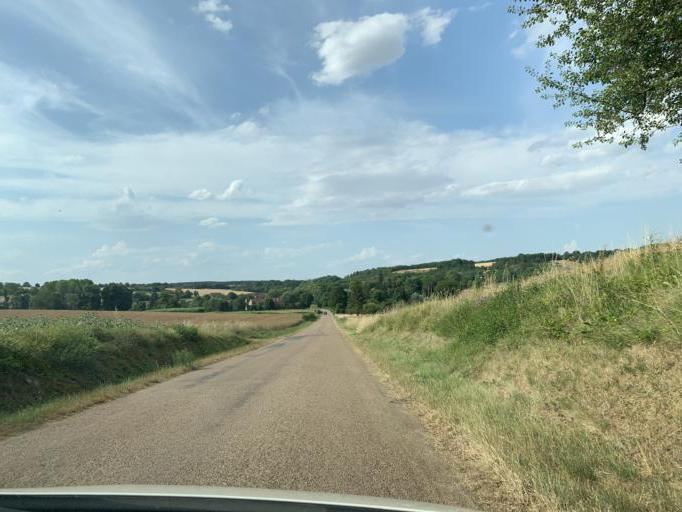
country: FR
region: Bourgogne
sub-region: Departement de l'Yonne
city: Fontenailles
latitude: 47.4758
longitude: 3.4221
